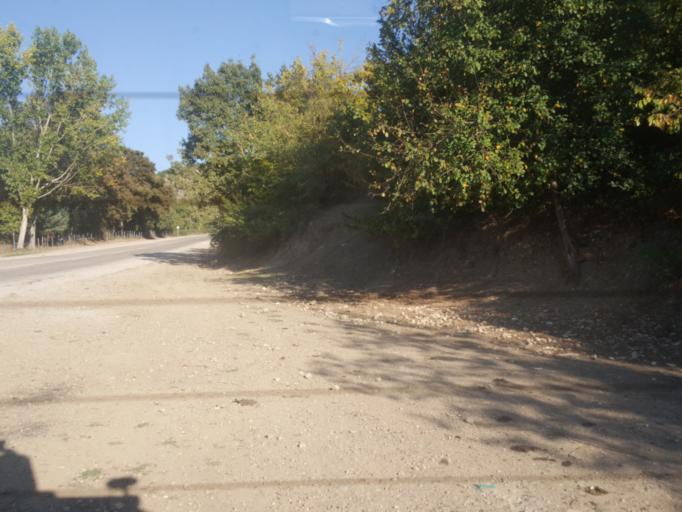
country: TR
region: Amasya
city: Tasova
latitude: 40.7390
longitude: 36.2754
